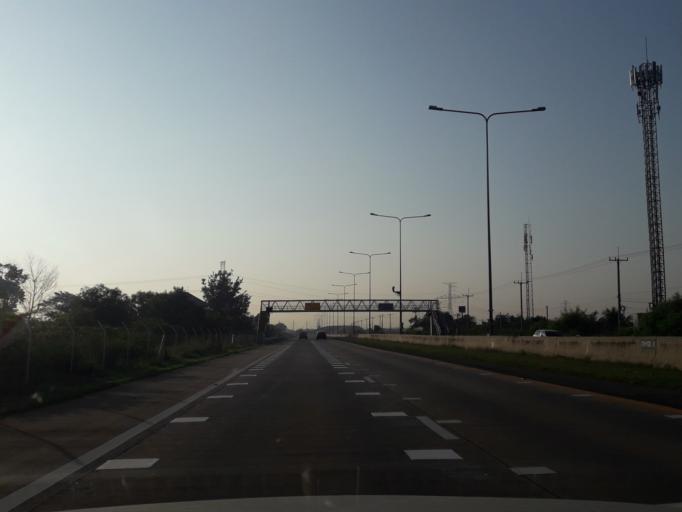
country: TH
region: Pathum Thani
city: Sam Khok
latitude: 14.1358
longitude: 100.5643
